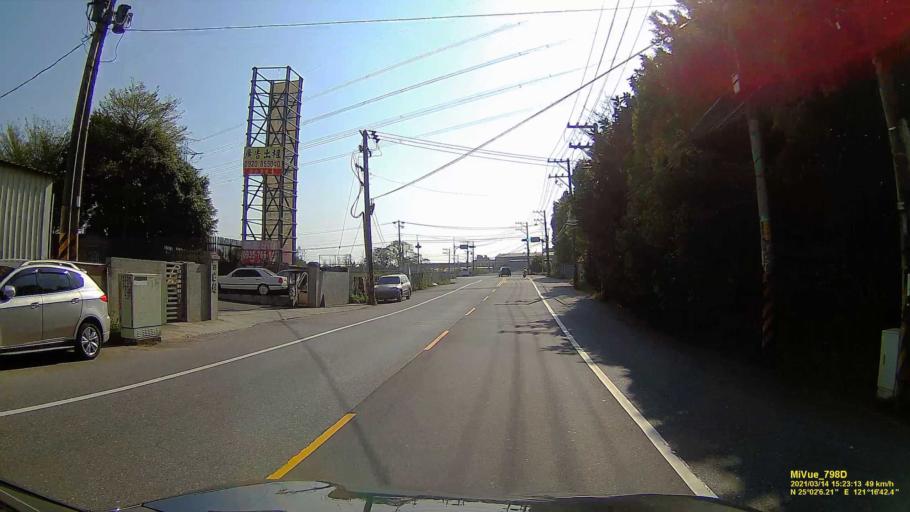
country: TW
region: Taiwan
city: Taoyuan City
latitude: 25.0349
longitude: 121.2783
